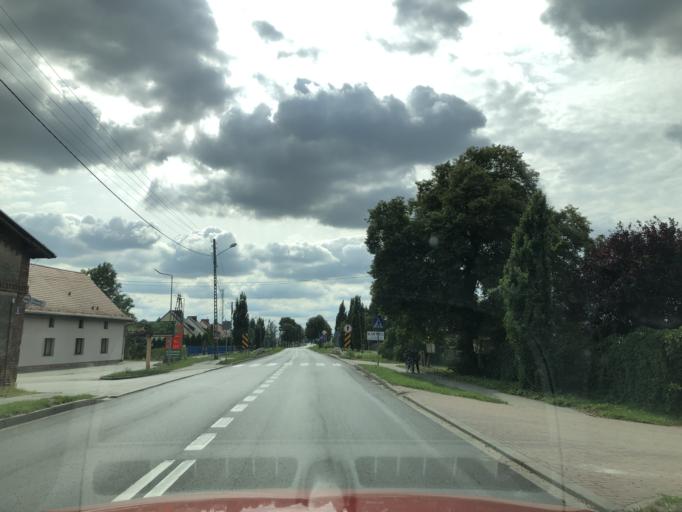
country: PL
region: Greater Poland Voivodeship
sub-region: Powiat szamotulski
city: Pniewy
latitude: 52.5051
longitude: 16.2488
